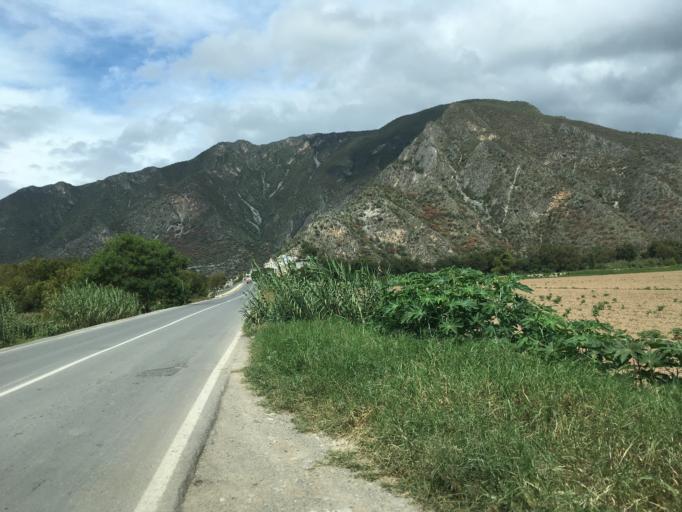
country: MX
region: Hidalgo
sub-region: San Agustin Metzquititlan
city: Mezquititlan
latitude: 20.5386
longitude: -98.7258
